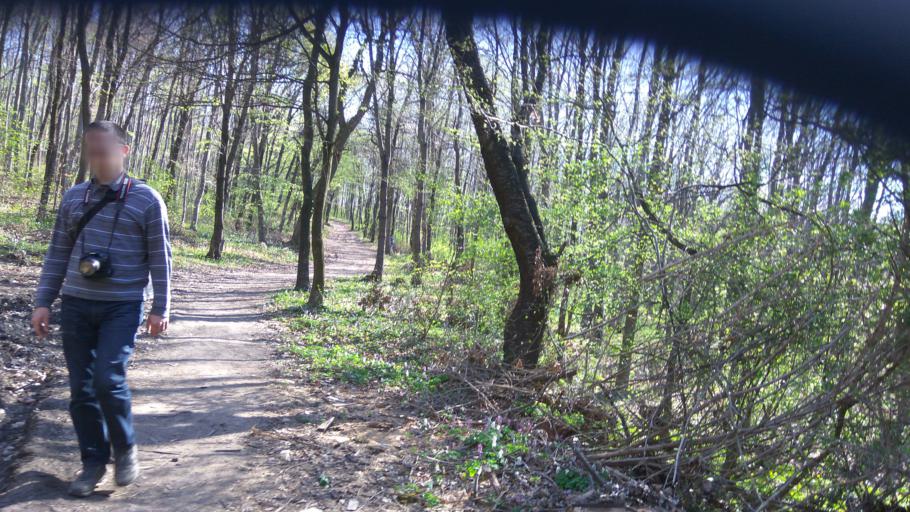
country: HU
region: Pest
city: Budaors
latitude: 47.4880
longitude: 18.9484
